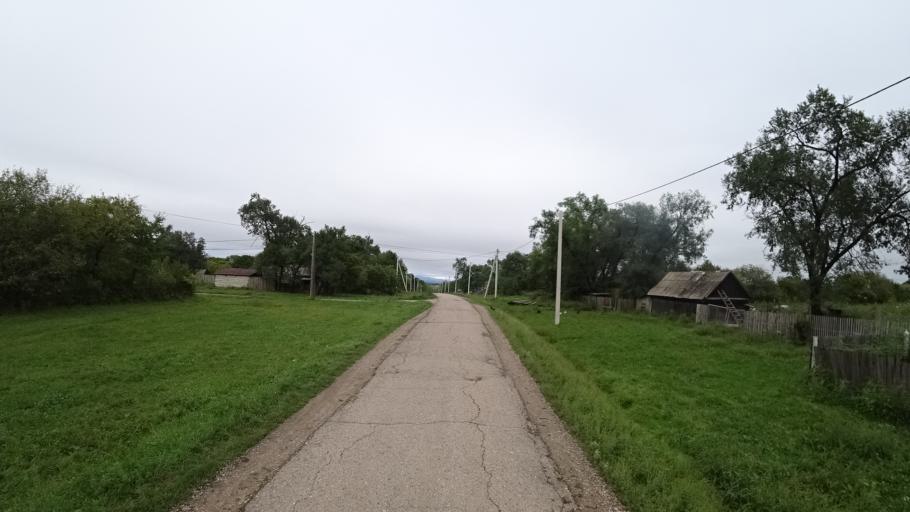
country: RU
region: Primorskiy
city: Monastyrishche
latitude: 44.0793
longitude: 132.5854
